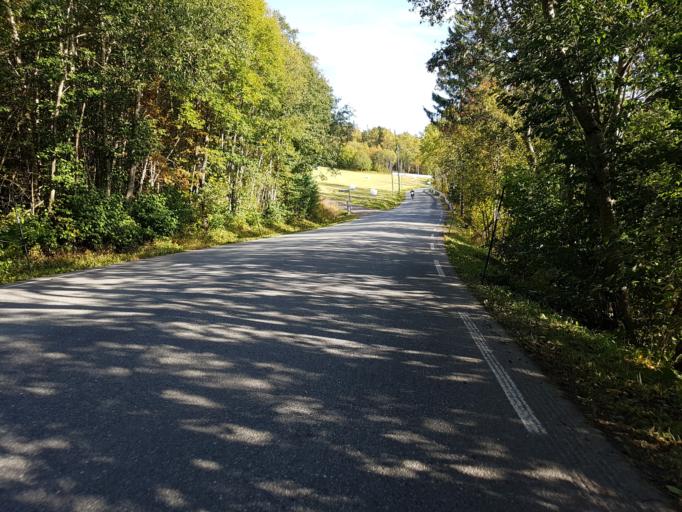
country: NO
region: Sor-Trondelag
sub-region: Malvik
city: Malvik
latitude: 63.3838
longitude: 10.5886
